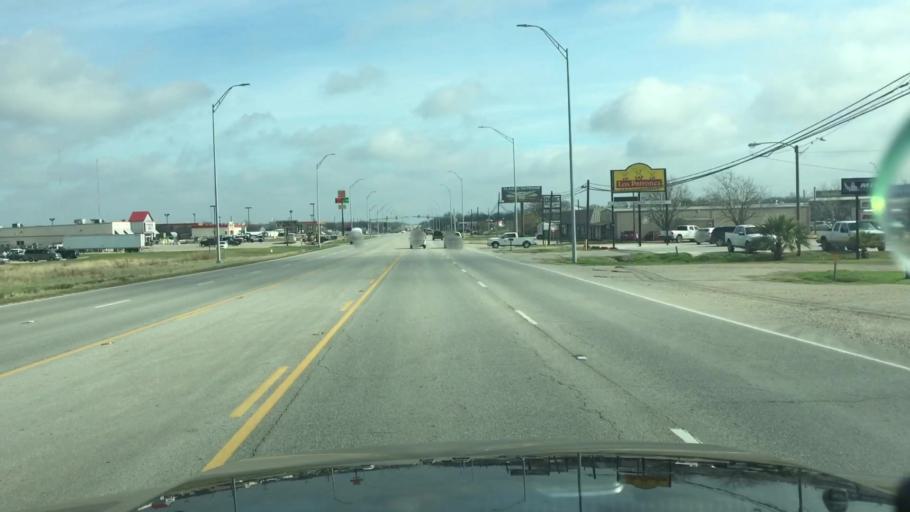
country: US
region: Texas
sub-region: Lee County
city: Giddings
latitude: 30.1788
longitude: -96.9109
